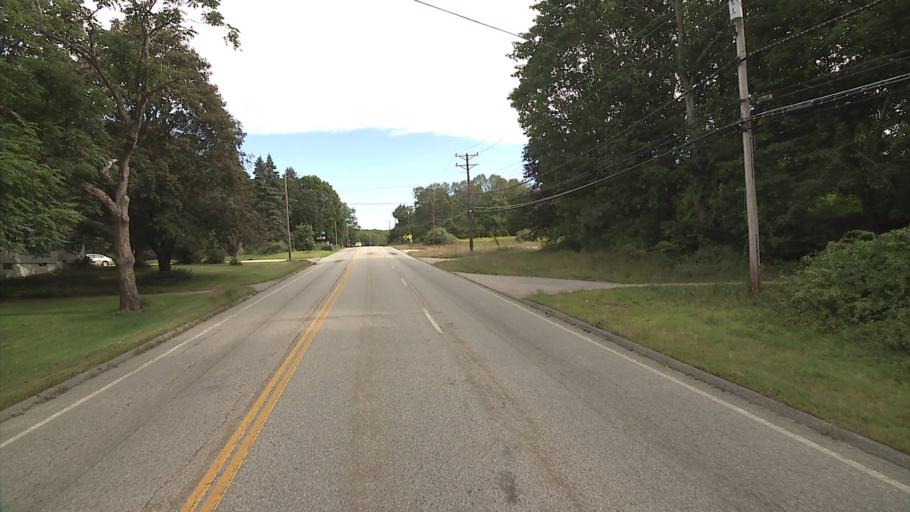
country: US
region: Connecticut
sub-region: New London County
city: Oxoboxo River
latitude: 41.4661
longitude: -72.1036
